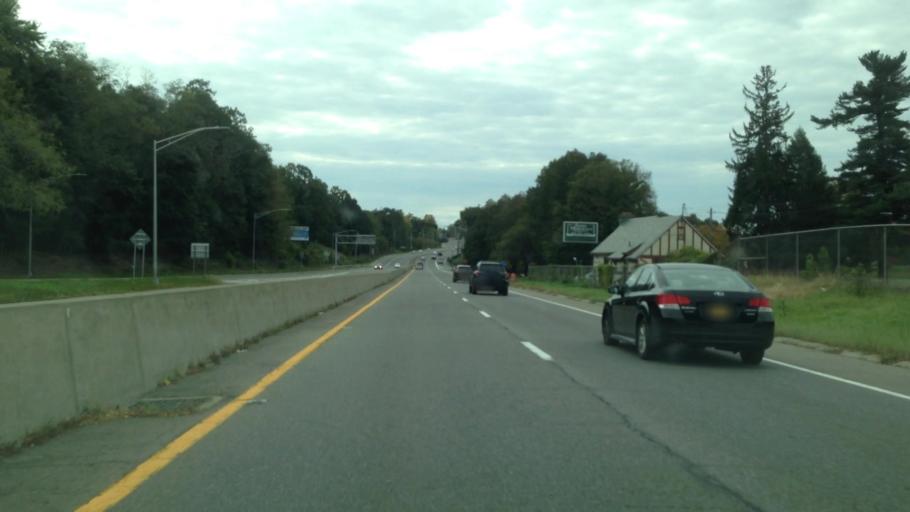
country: US
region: New York
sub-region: Dutchess County
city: Poughkeepsie
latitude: 41.6862
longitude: -73.9306
